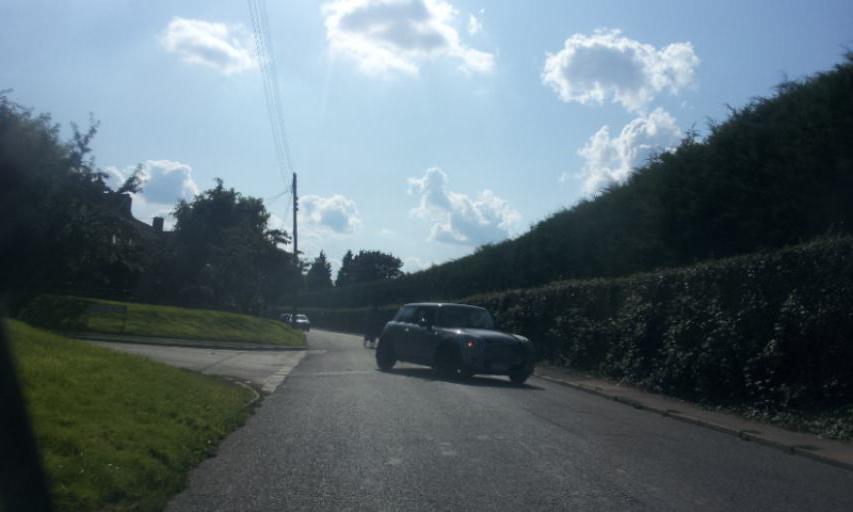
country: GB
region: England
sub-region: Kent
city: East Peckham
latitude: 51.2155
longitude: 0.3806
